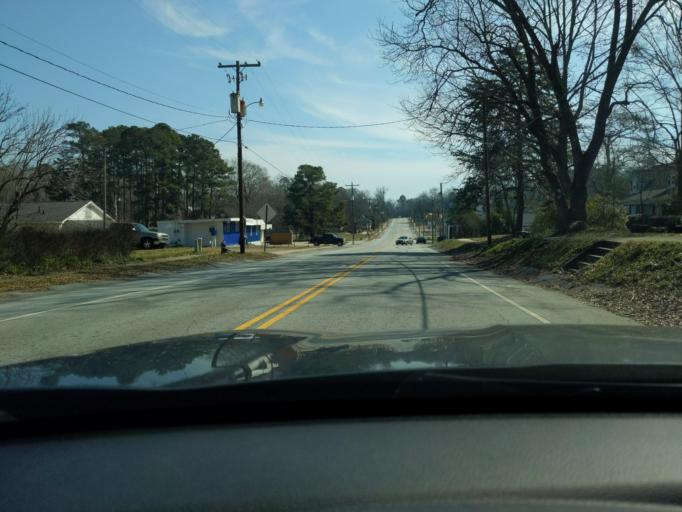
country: US
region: South Carolina
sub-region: Abbeville County
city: Calhoun Falls
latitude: 34.0917
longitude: -82.5948
